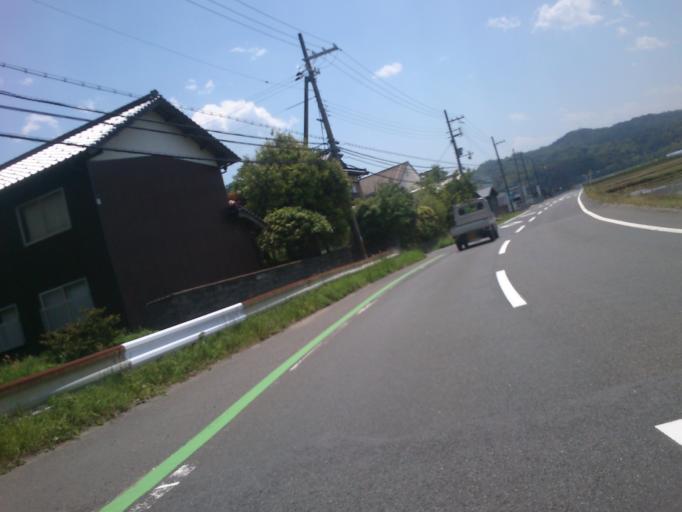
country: JP
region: Kyoto
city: Miyazu
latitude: 35.7258
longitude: 135.1066
